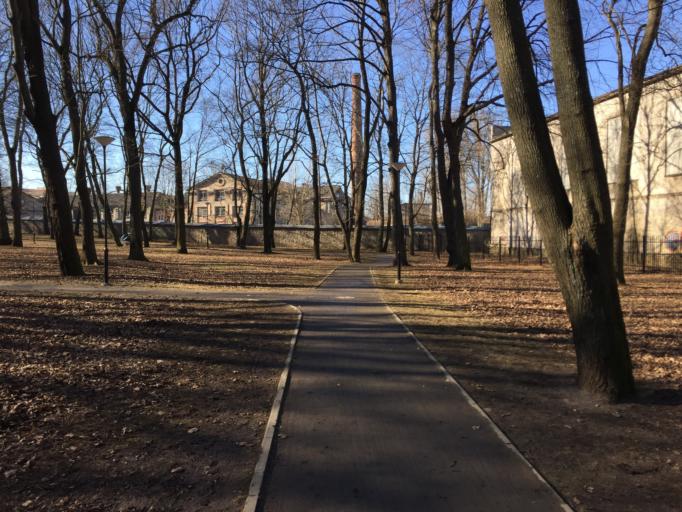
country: EE
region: Harju
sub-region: Tallinna linn
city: Tallinn
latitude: 59.4504
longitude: 24.7300
